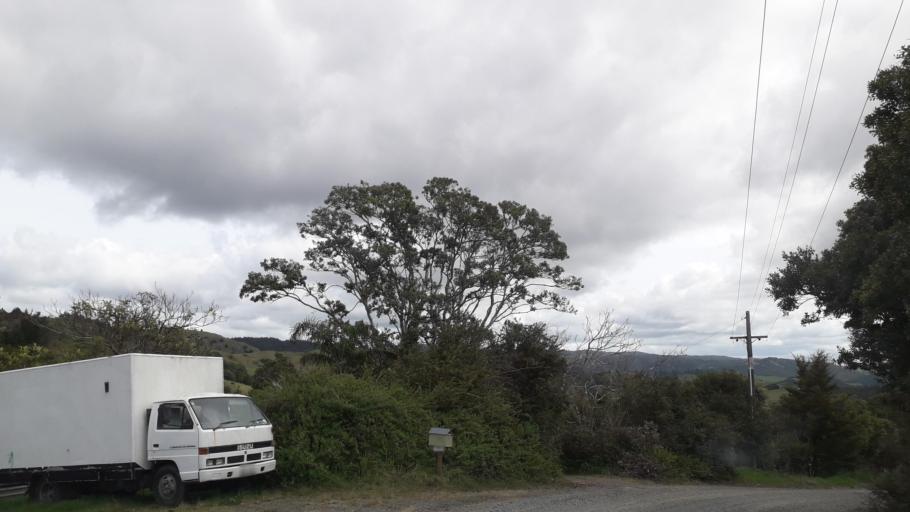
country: NZ
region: Northland
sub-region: Far North District
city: Kerikeri
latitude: -35.1248
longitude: 173.7460
